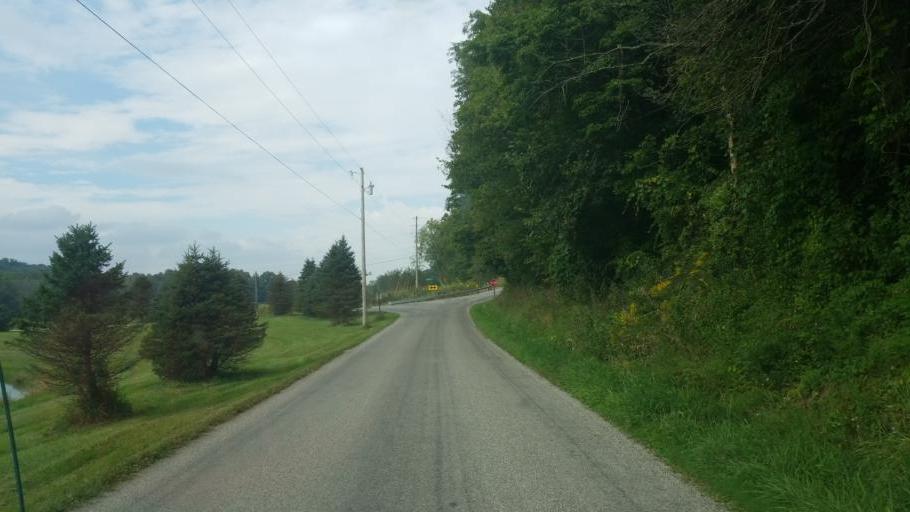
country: US
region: Ohio
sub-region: Wayne County
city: West Salem
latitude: 40.9095
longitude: -82.0063
